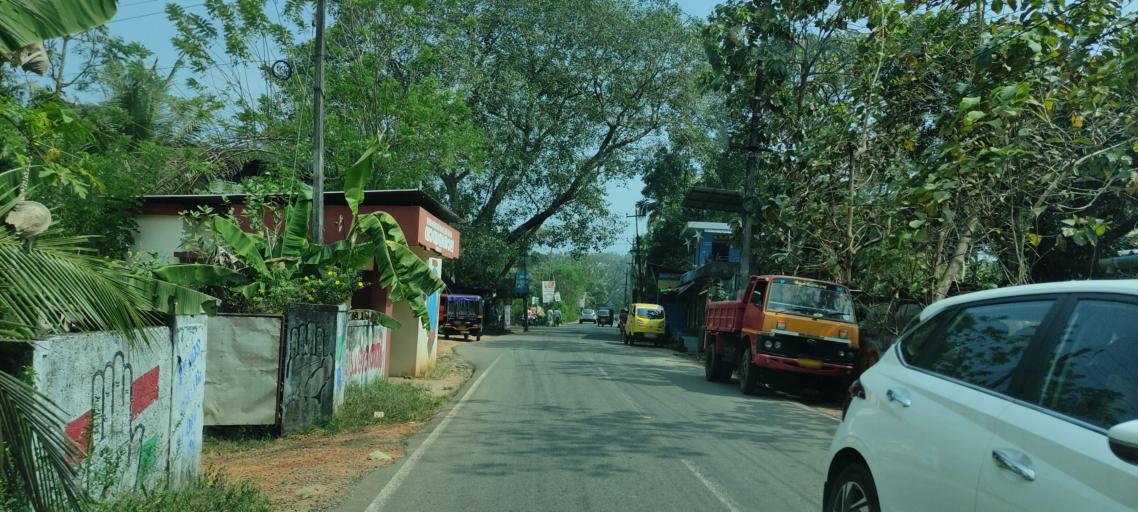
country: IN
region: Kerala
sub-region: Alappuzha
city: Shertallai
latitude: 9.6553
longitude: 76.3510
